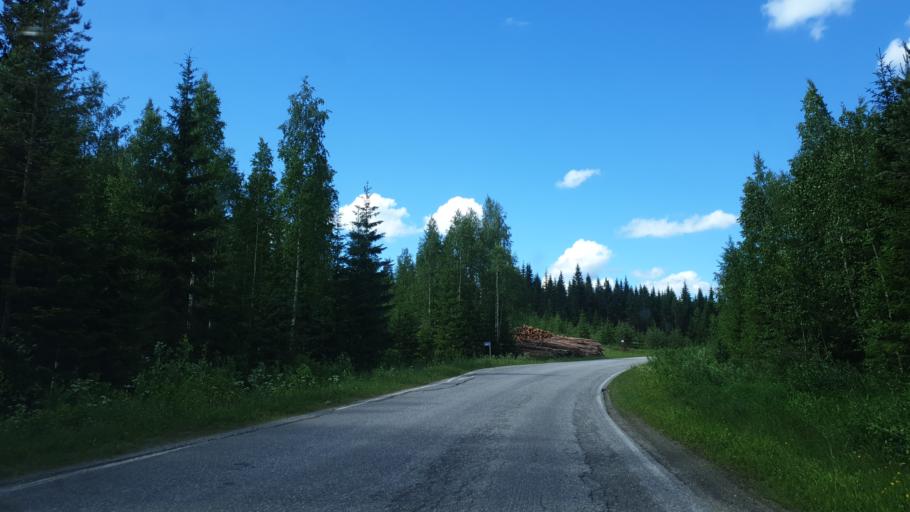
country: FI
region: Northern Savo
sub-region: Koillis-Savo
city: Kaavi
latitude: 63.0278
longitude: 28.6137
